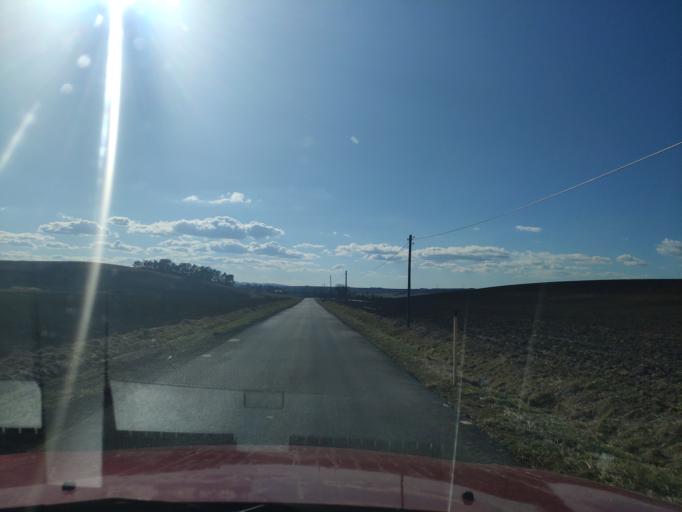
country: HU
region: Borsod-Abauj-Zemplen
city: Putnok
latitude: 48.3658
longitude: 20.3392
